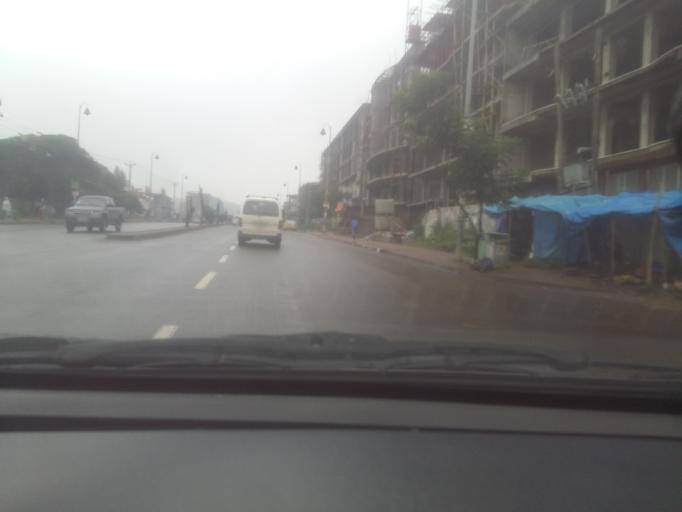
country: ET
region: Adis Abeba
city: Addis Ababa
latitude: 8.9522
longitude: 38.7166
